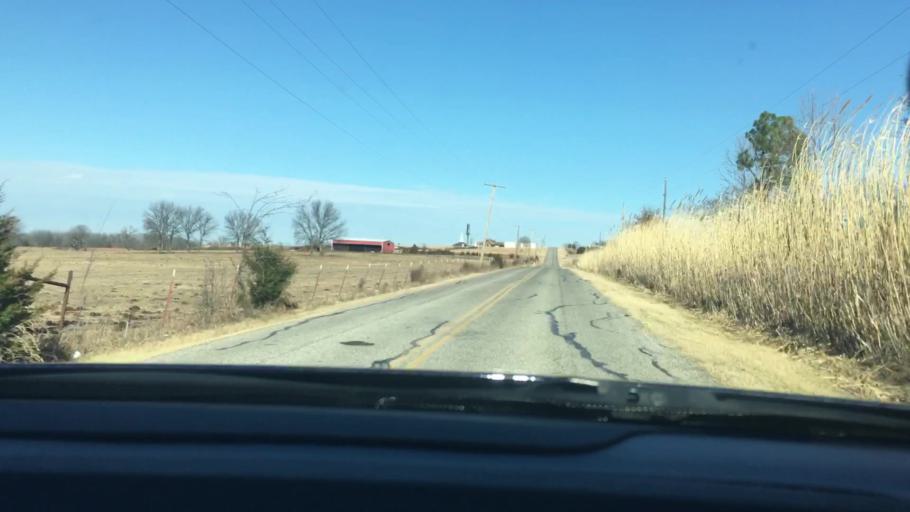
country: US
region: Oklahoma
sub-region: Murray County
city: Davis
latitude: 34.4988
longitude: -97.0553
